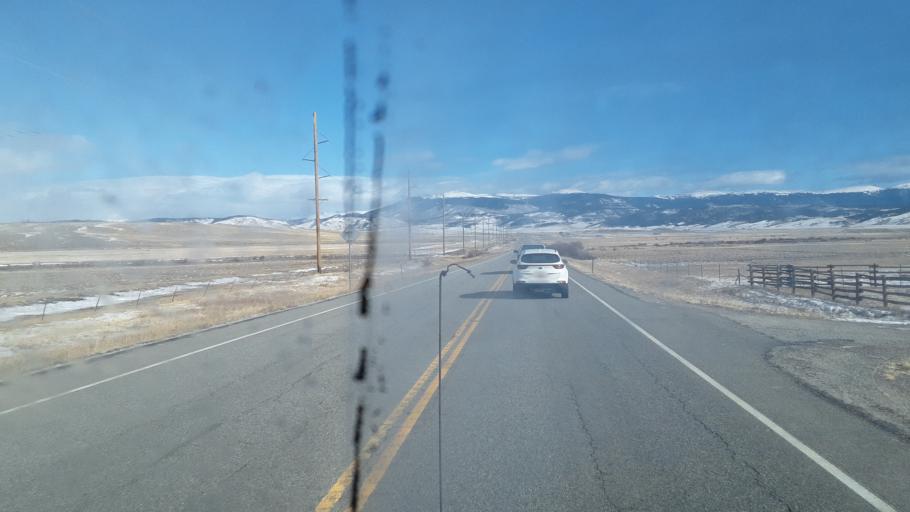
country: US
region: Colorado
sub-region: Park County
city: Fairplay
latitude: 39.3487
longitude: -105.8359
